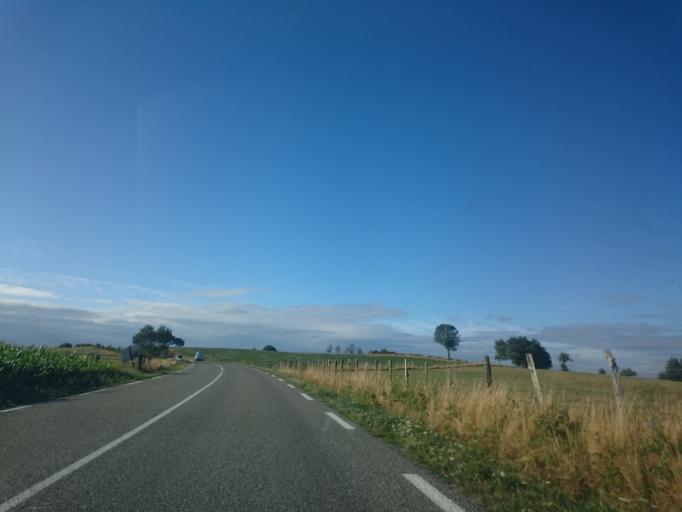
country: FR
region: Midi-Pyrenees
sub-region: Departement de l'Aveyron
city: Entraygues-sur-Truyere
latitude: 44.7356
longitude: 2.5089
